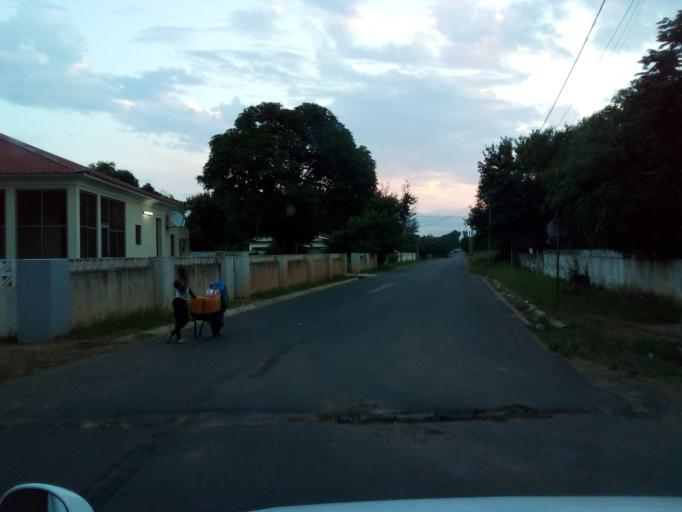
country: MZ
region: Maputo City
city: Maputo
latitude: -26.3454
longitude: 32.6765
